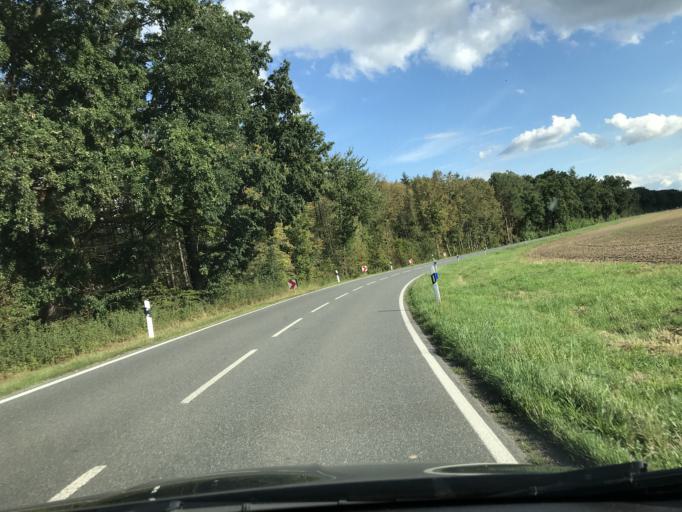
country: DE
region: Hesse
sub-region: Regierungsbezirk Darmstadt
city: Munster
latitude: 49.9125
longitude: 8.9135
